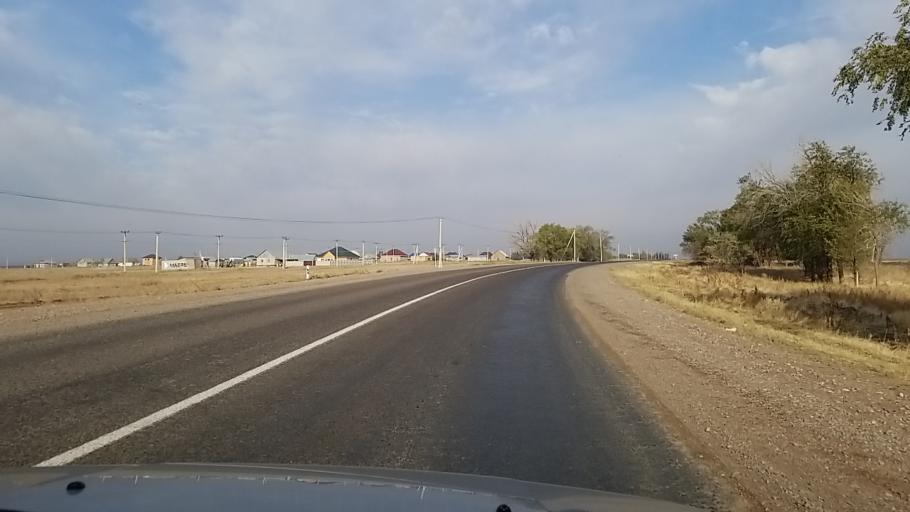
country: KZ
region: Almaty Oblysy
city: Burunday
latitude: 43.4783
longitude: 76.6802
